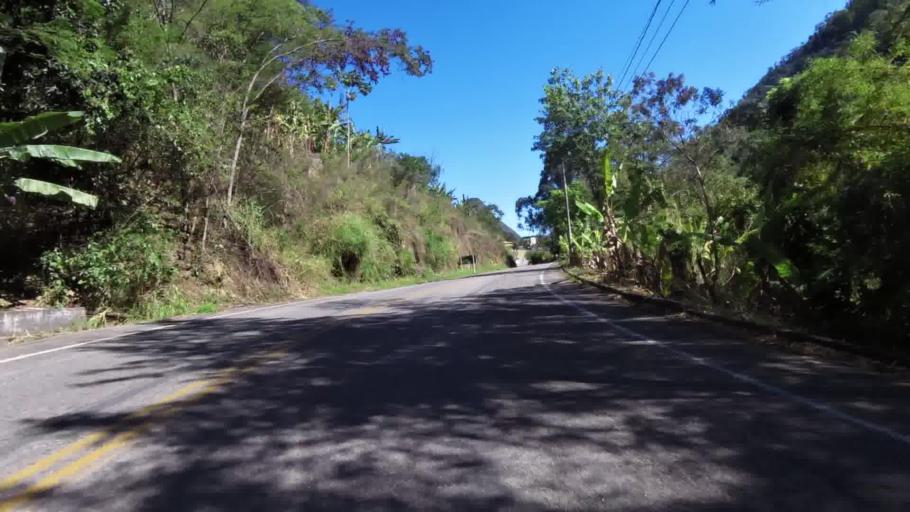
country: BR
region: Espirito Santo
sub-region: Iconha
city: Iconha
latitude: -20.7393
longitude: -40.8694
